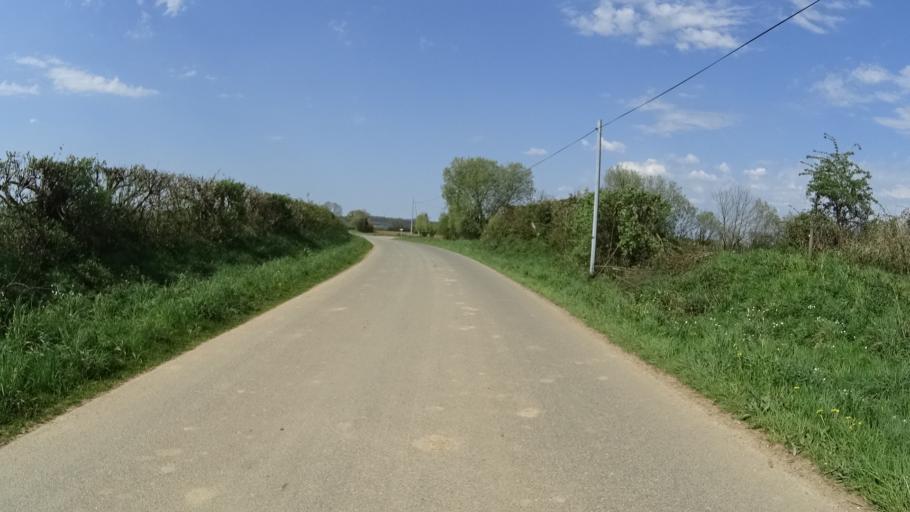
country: FR
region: Brittany
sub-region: Departement du Finistere
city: Sizun
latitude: 48.4190
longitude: -4.0864
